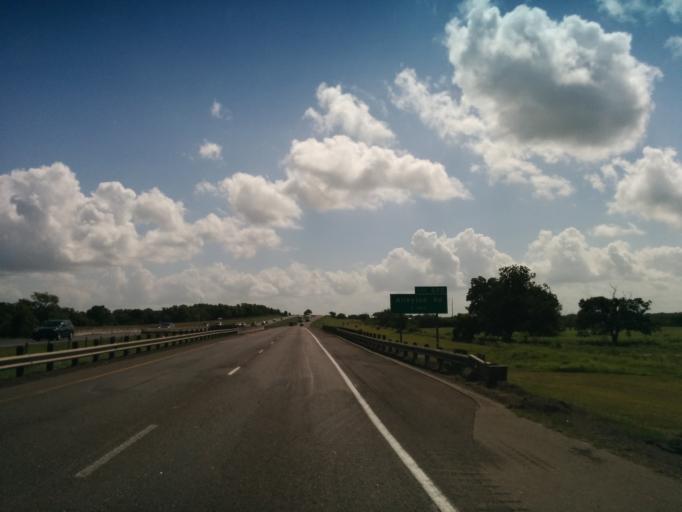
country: US
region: Texas
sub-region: Colorado County
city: Columbus
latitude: 29.7004
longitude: -96.5242
